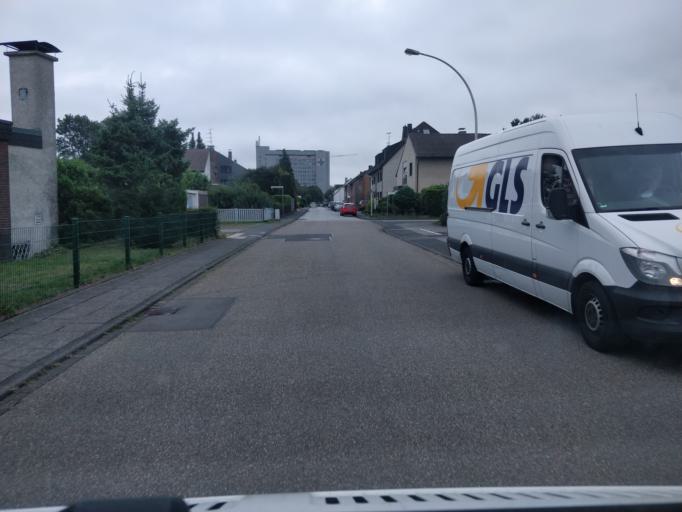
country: DE
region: North Rhine-Westphalia
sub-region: Regierungsbezirk Koln
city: Frechen
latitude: 50.9270
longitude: 6.8078
